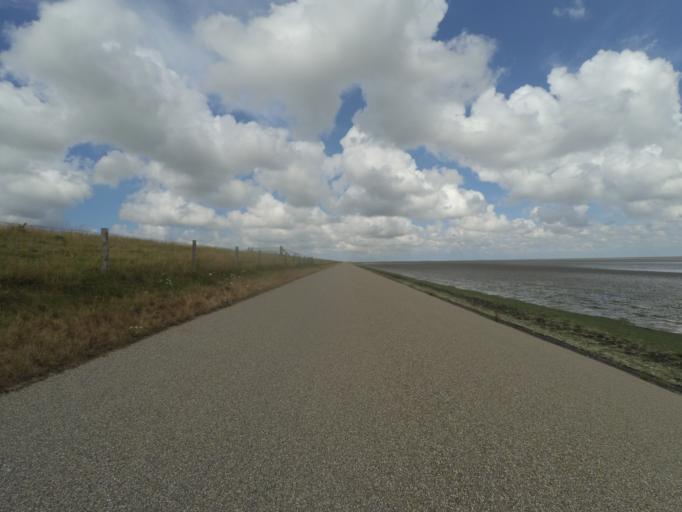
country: NL
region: North Holland
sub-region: Gemeente Texel
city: Den Burg
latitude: 53.1099
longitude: 4.8986
